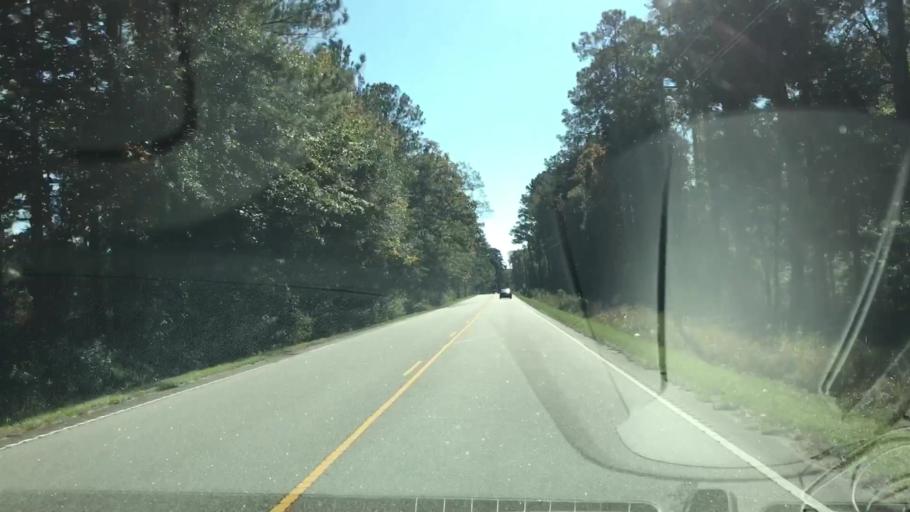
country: US
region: South Carolina
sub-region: Jasper County
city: Ridgeland
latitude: 32.4847
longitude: -80.8859
